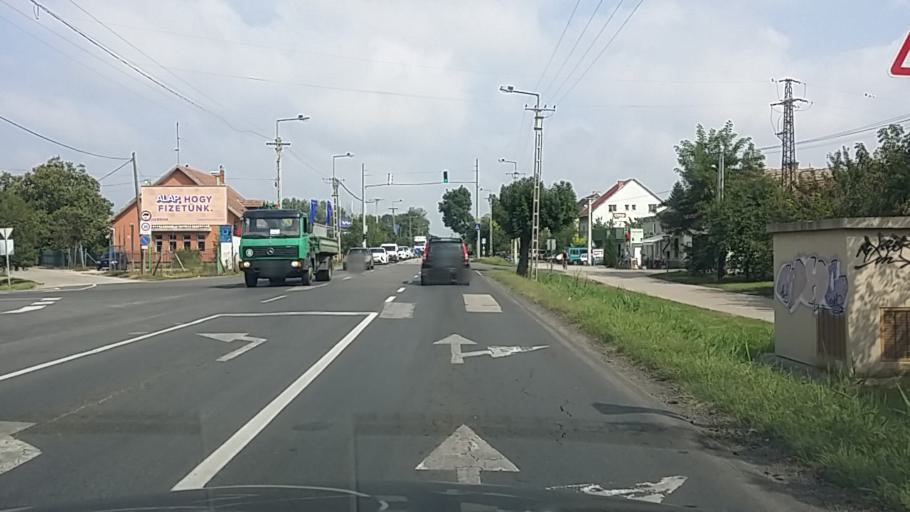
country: HU
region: Csongrad
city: Szeged
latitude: 46.2805
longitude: 20.1685
